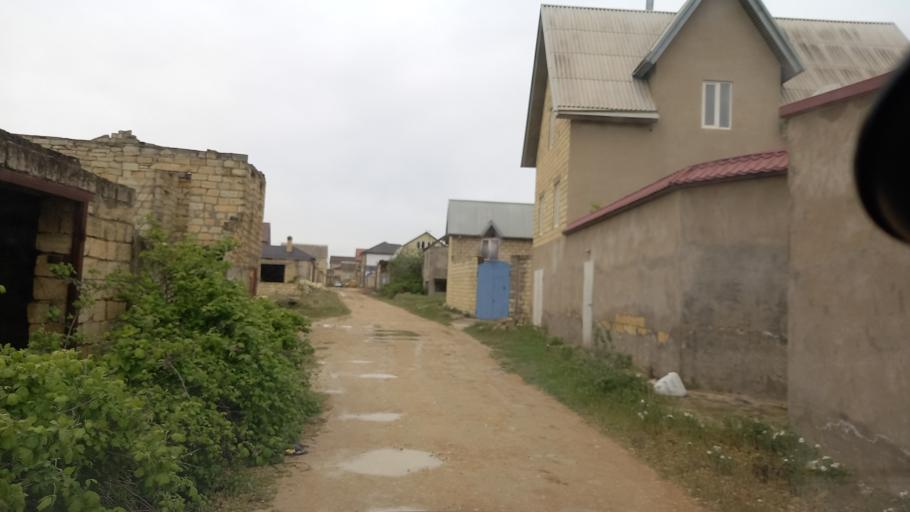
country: RU
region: Dagestan
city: Sabnova
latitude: 42.1210
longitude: 48.2633
